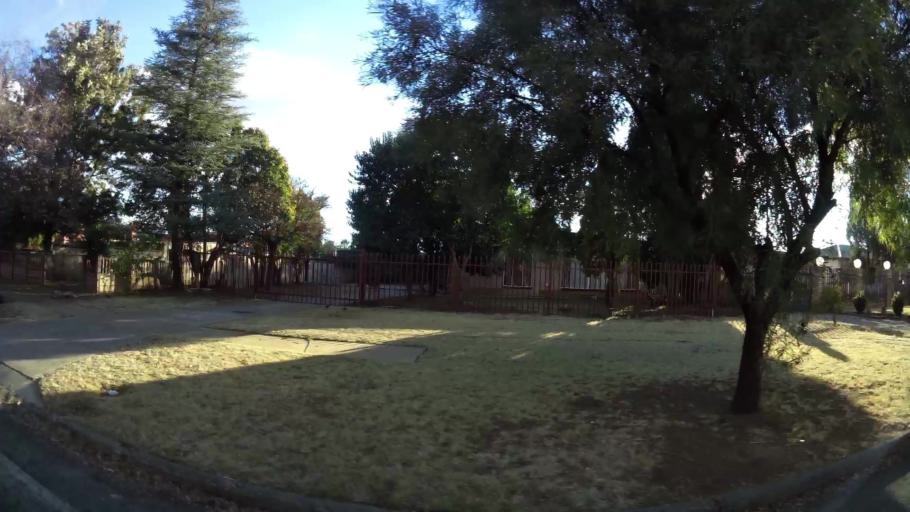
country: ZA
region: North-West
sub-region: Dr Kenneth Kaunda District Municipality
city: Potchefstroom
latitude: -26.7400
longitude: 27.0887
